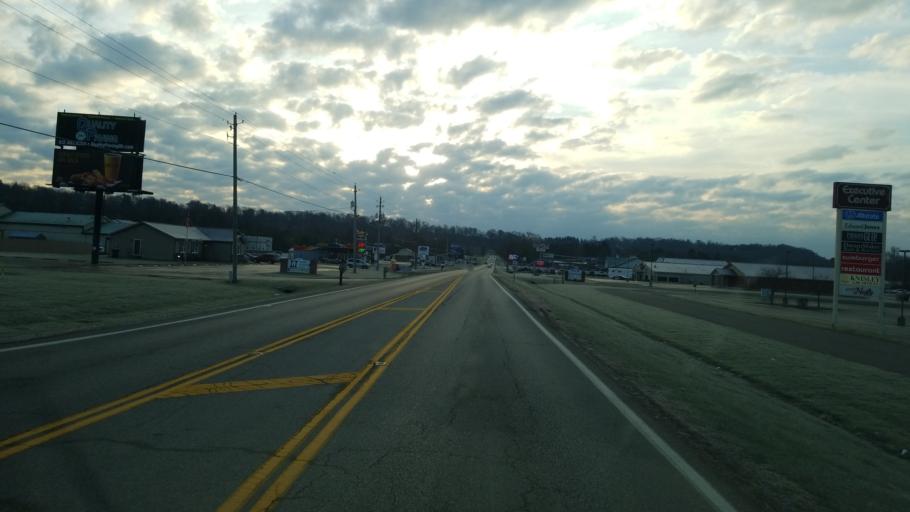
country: US
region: Ohio
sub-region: Ross County
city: North Fork Village
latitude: 39.3452
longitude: -83.0383
